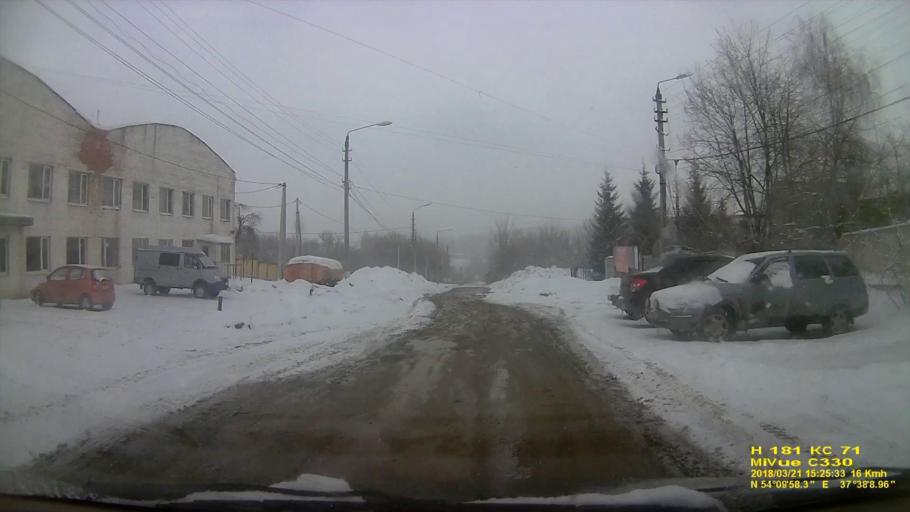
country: RU
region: Tula
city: Tula
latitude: 54.1662
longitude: 37.6357
